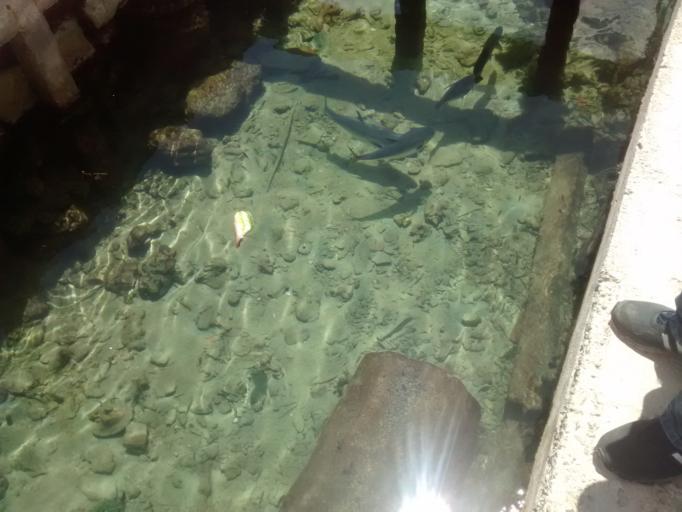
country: CO
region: Sucre
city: San Onofre
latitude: 9.7861
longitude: -75.8584
